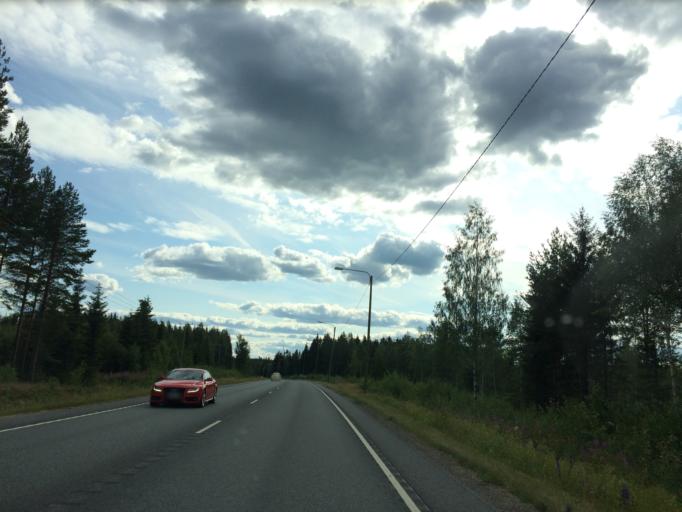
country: FI
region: Haeme
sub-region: Haemeenlinna
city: Janakkala
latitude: 60.9203
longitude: 24.5785
